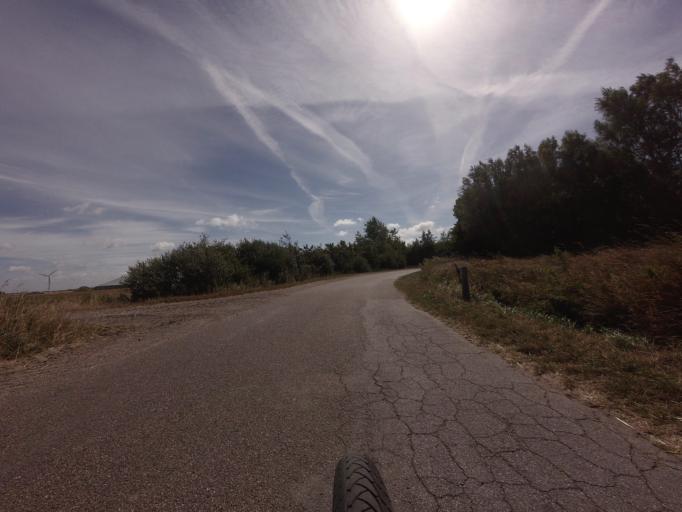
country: DK
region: North Denmark
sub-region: Hjorring Kommune
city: Vra
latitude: 57.3397
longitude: 9.8086
